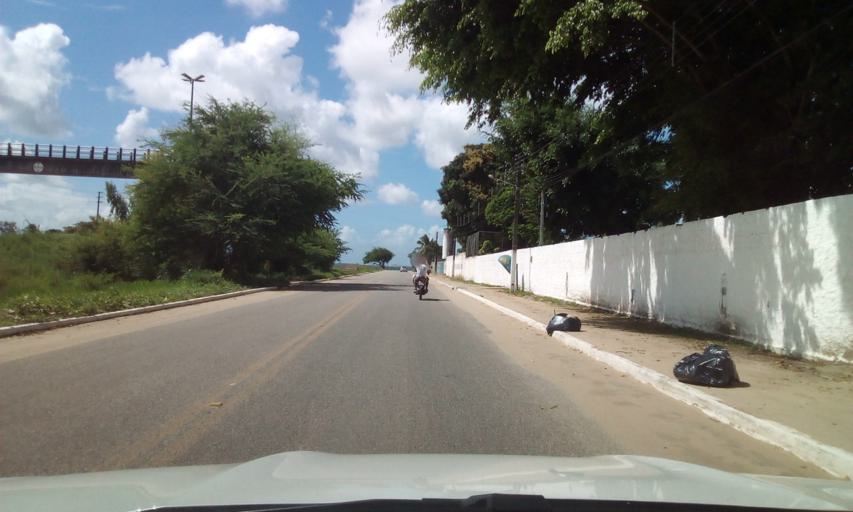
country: BR
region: Paraiba
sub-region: Bayeux
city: Bayeux
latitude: -7.1283
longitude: -34.9516
